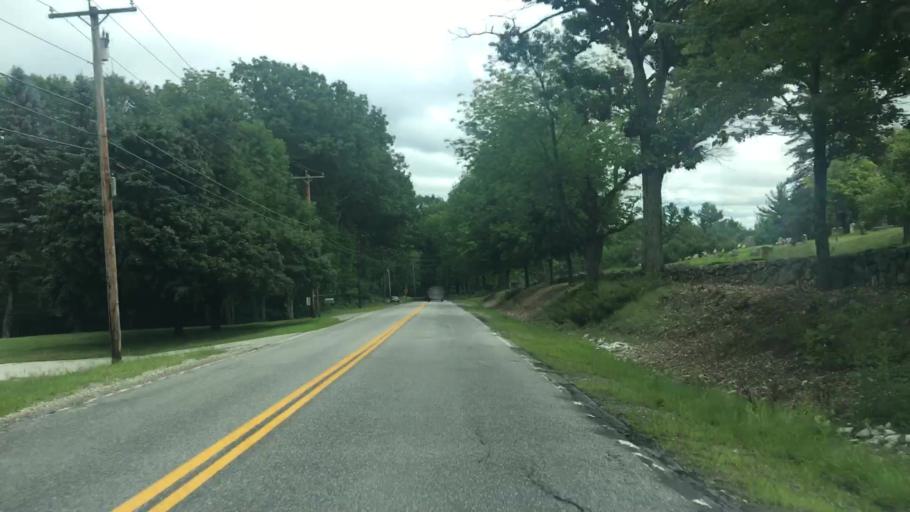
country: US
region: Maine
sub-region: York County
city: Limerick
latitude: 43.6819
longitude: -70.7893
